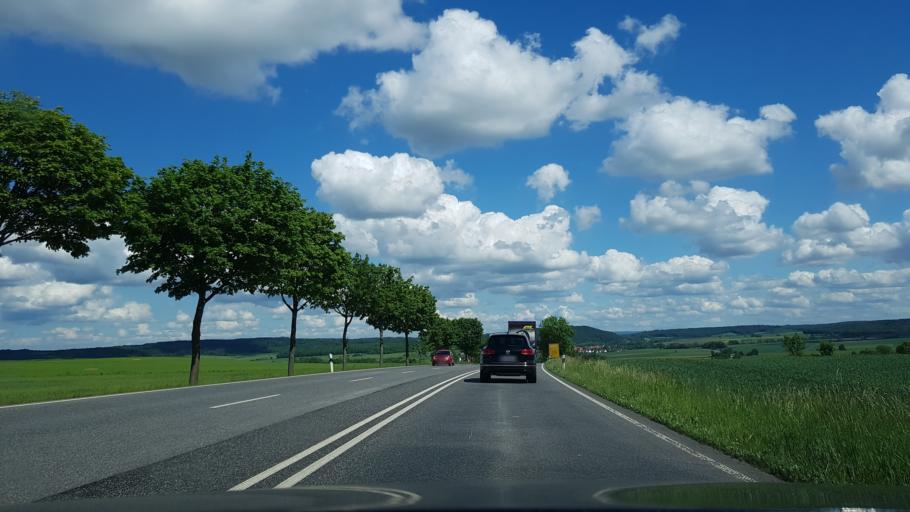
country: DE
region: Hesse
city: Liebenau
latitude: 51.4440
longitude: 9.2849
